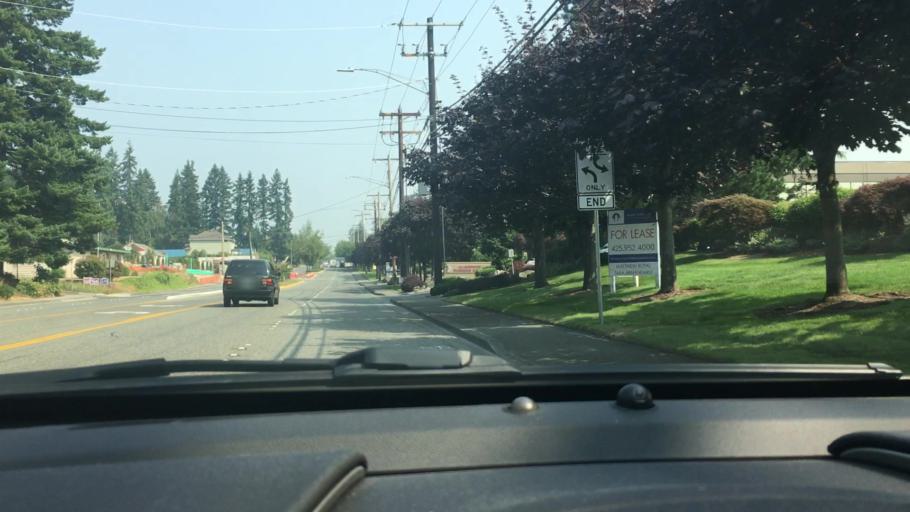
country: US
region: Washington
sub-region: Snohomish County
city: Alderwood Manor
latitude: 47.8246
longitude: -122.2817
